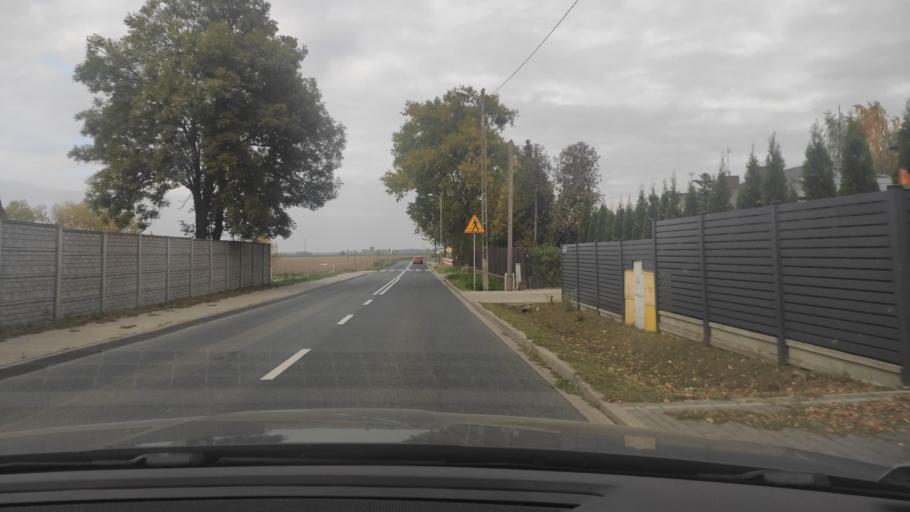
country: PL
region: Greater Poland Voivodeship
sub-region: Powiat poznanski
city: Swarzedz
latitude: 52.4262
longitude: 17.1579
